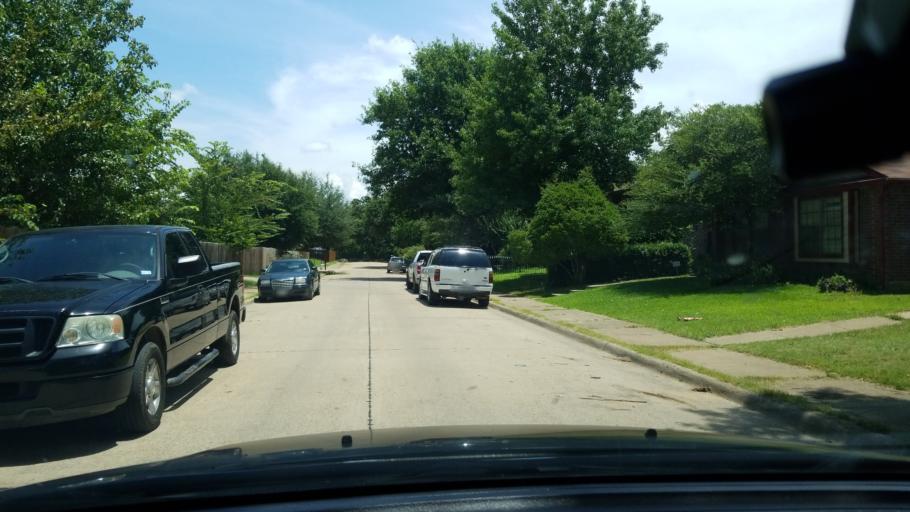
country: US
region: Texas
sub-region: Dallas County
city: Balch Springs
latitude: 32.7514
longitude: -96.6424
